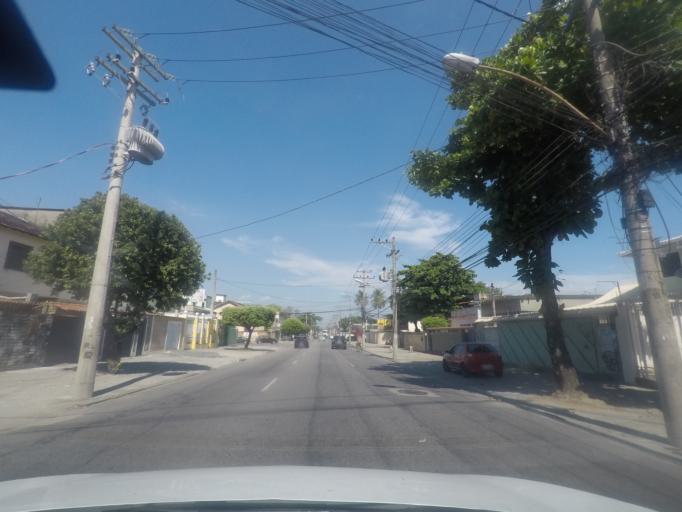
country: BR
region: Rio de Janeiro
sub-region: Nilopolis
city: Nilopolis
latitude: -22.8796
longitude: -43.4605
